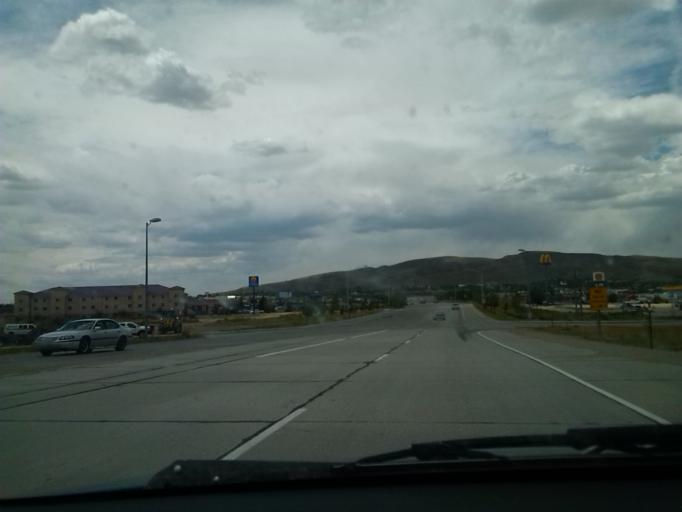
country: US
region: Wyoming
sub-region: Carbon County
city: Rawlins
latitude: 41.7920
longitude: -107.2081
